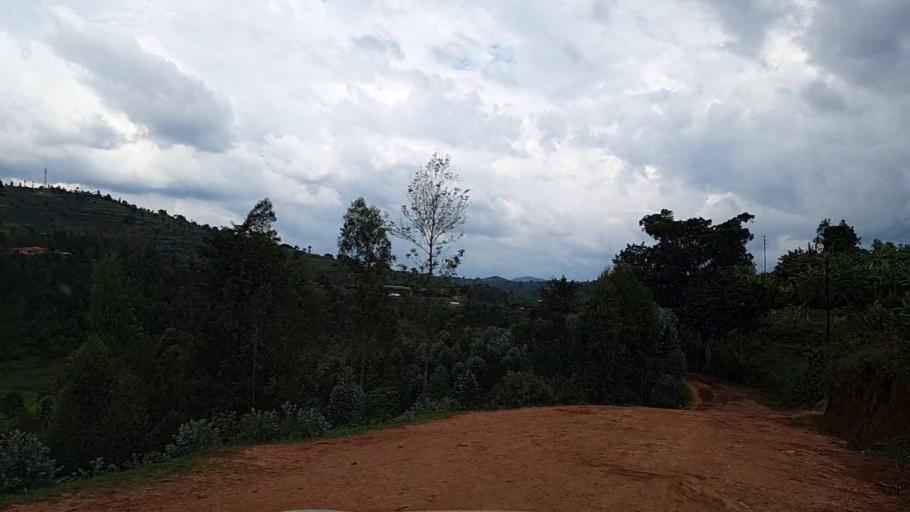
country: RW
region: Southern Province
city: Gikongoro
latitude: -2.4161
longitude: 29.6582
